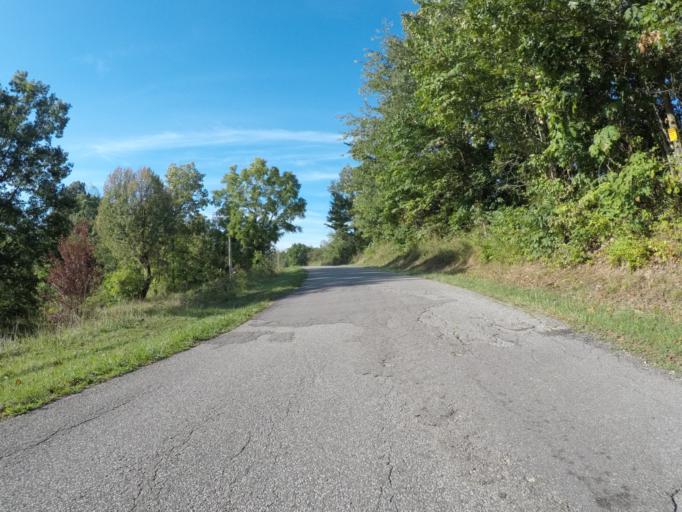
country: US
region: Ohio
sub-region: Lawrence County
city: Coal Grove
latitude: 38.6003
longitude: -82.5557
